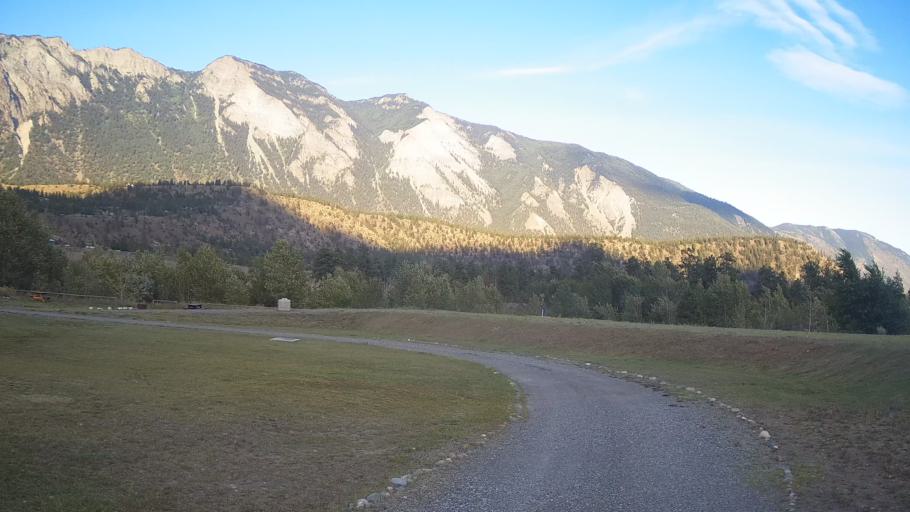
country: CA
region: British Columbia
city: Lillooet
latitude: 50.6805
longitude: -121.9313
